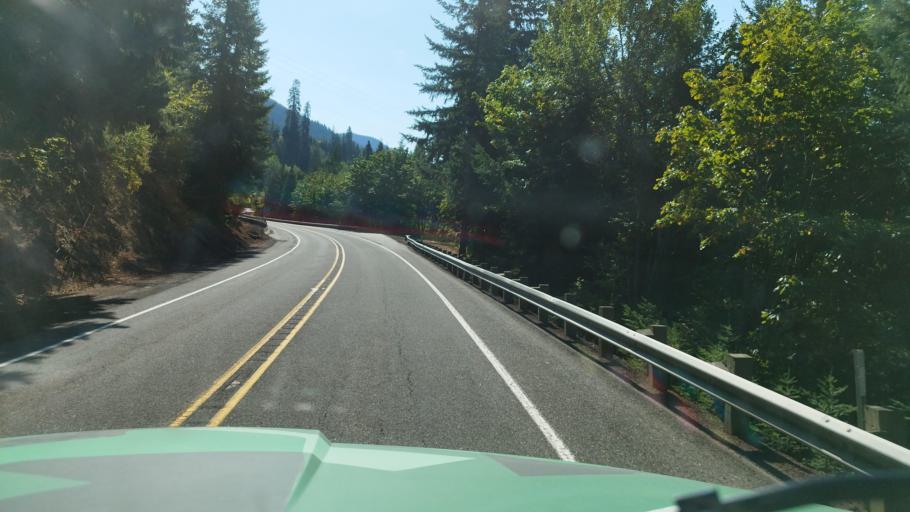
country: US
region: Oregon
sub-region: Hood River County
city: Odell
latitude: 45.5052
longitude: -121.5638
